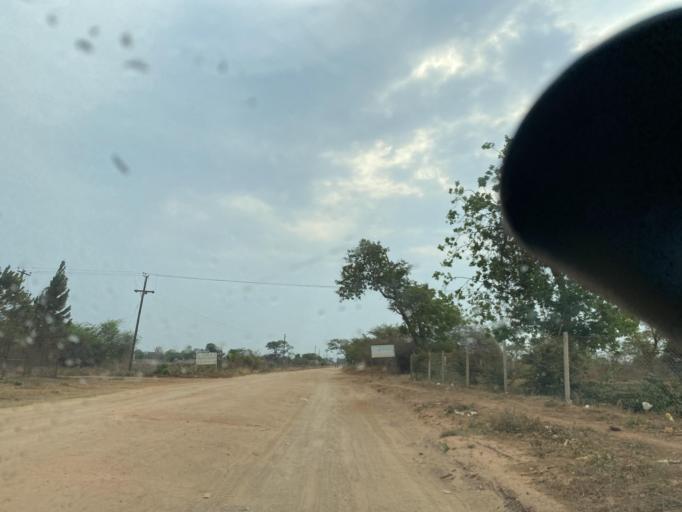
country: ZM
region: Lusaka
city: Lusaka
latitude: -15.2880
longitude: 28.2884
